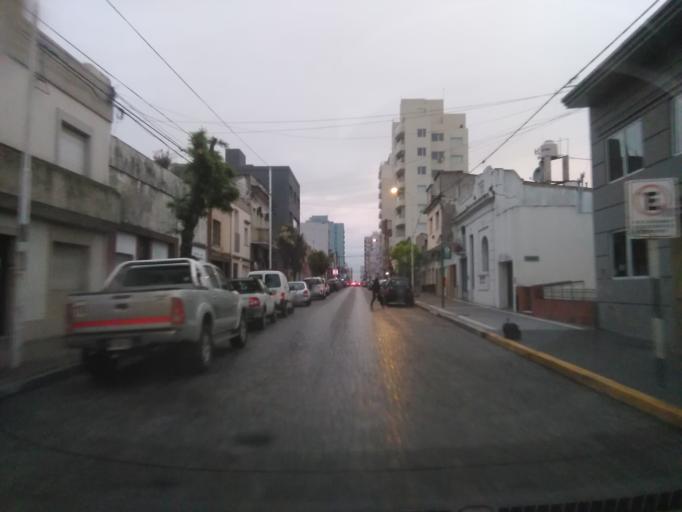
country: AR
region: Buenos Aires
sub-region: Partido de Tandil
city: Tandil
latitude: -37.3266
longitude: -59.1411
